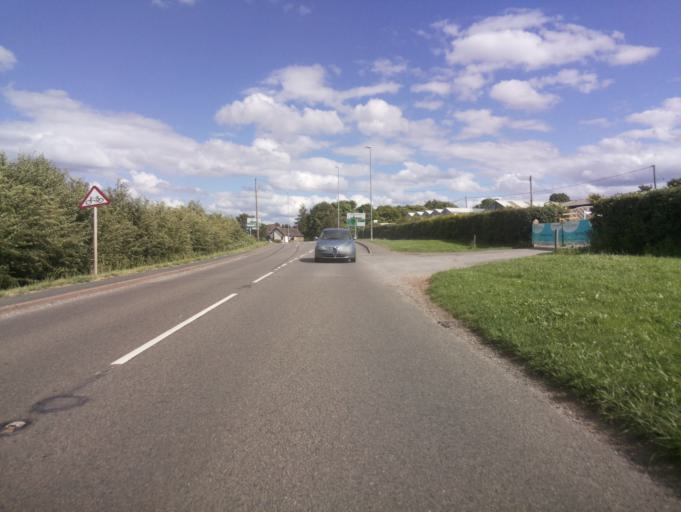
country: GB
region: England
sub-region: Leicestershire
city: Hathern
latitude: 52.8002
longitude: -1.2642
